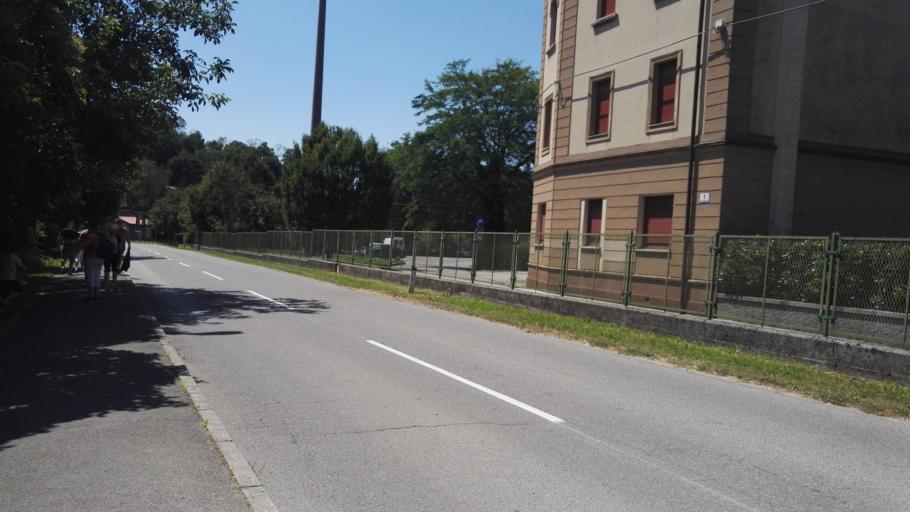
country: SI
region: Nova Gorica
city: Nova Gorica
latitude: 45.9538
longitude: 13.6346
